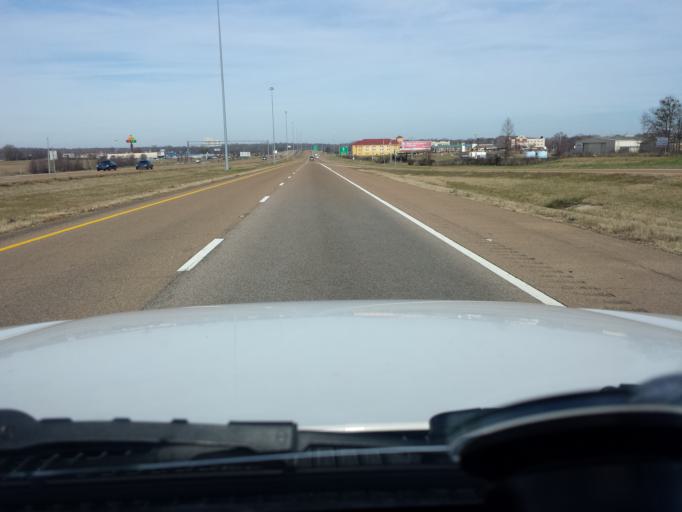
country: US
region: Mississippi
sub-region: Madison County
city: Canton
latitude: 32.5951
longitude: -90.0691
